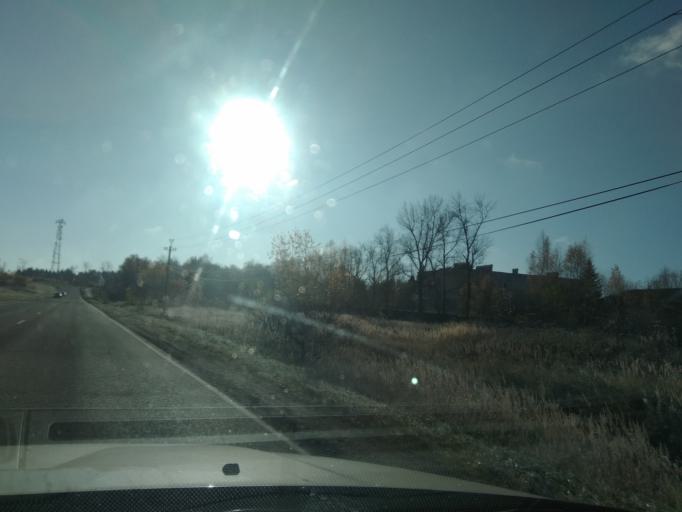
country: RU
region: Moskovskaya
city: Istra
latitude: 55.8775
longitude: 36.8493
